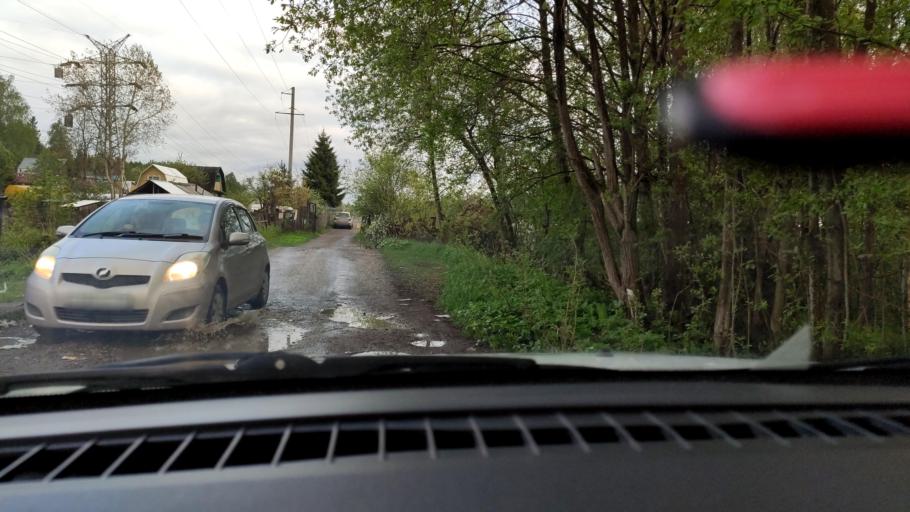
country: RU
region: Perm
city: Polazna
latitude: 58.1339
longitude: 56.4098
